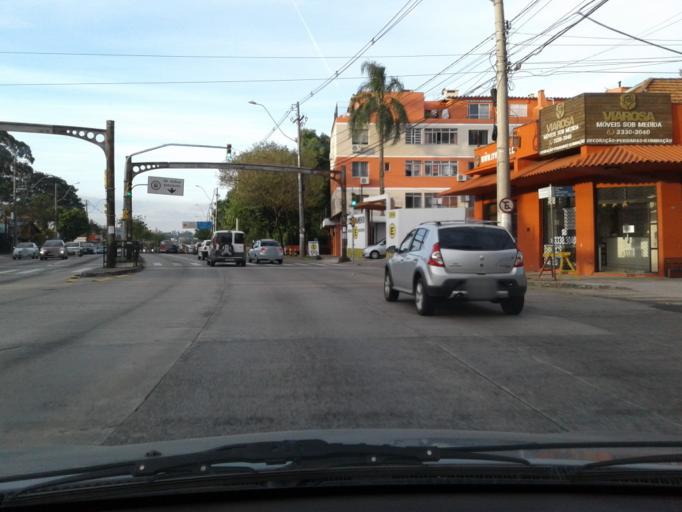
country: BR
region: Rio Grande do Sul
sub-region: Porto Alegre
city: Porto Alegre
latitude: -30.0811
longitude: -51.2105
